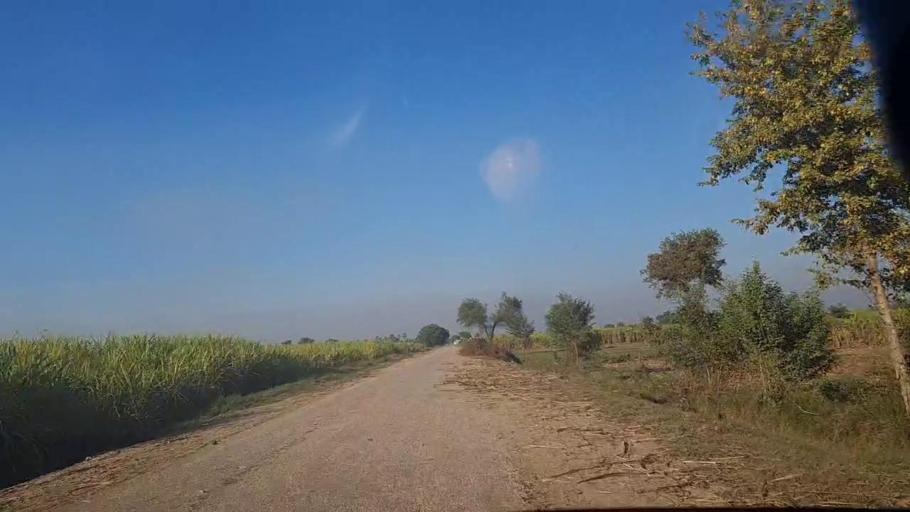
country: PK
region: Sindh
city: Sobhadero
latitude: 27.4119
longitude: 68.4226
